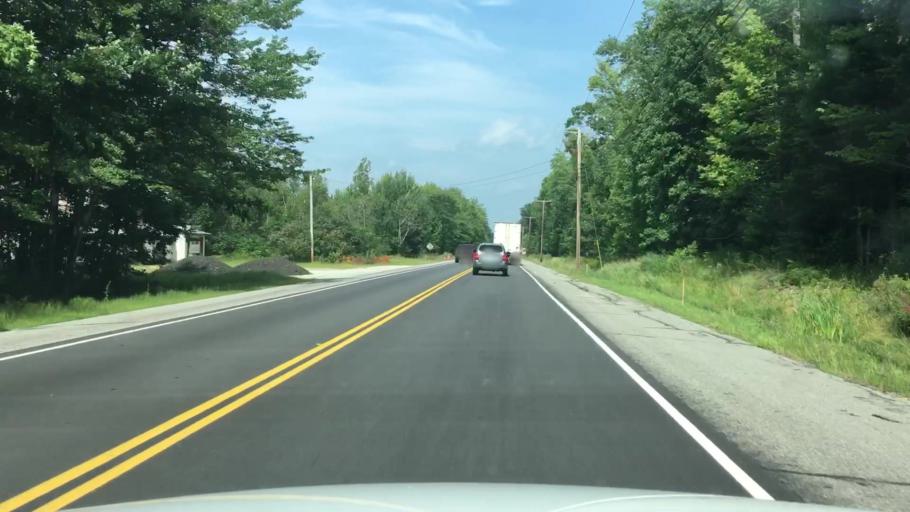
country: US
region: Maine
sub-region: Androscoggin County
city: Turner
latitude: 44.2173
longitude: -70.2464
